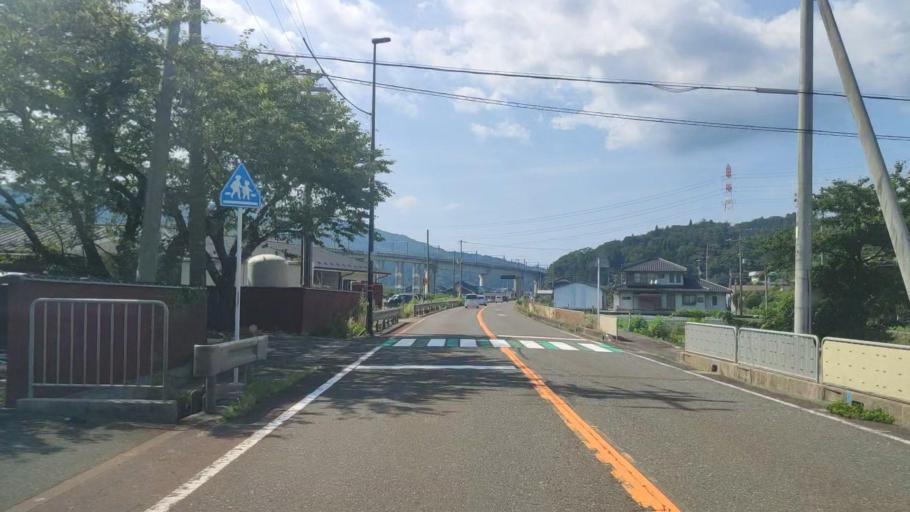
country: JP
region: Fukui
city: Tsuruga
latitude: 35.5277
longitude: 136.1577
